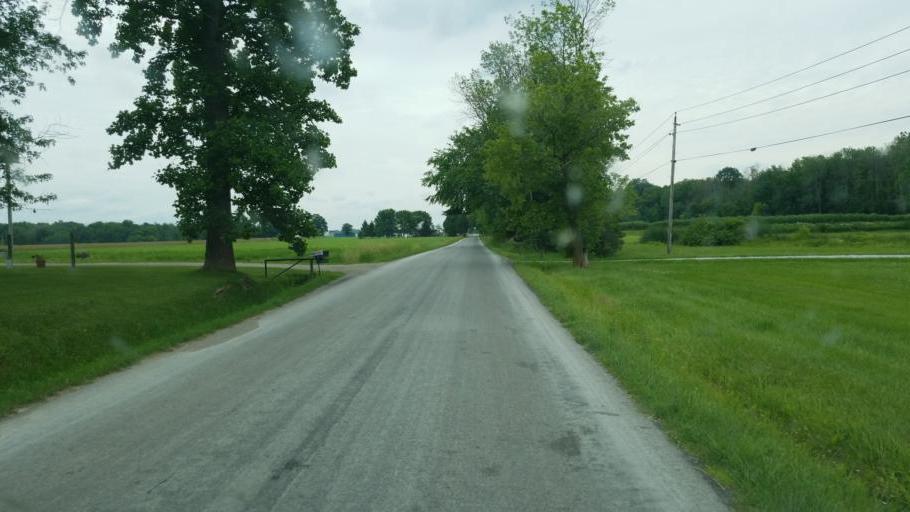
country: US
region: Ohio
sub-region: Geauga County
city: Middlefield
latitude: 41.4939
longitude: -81.0383
